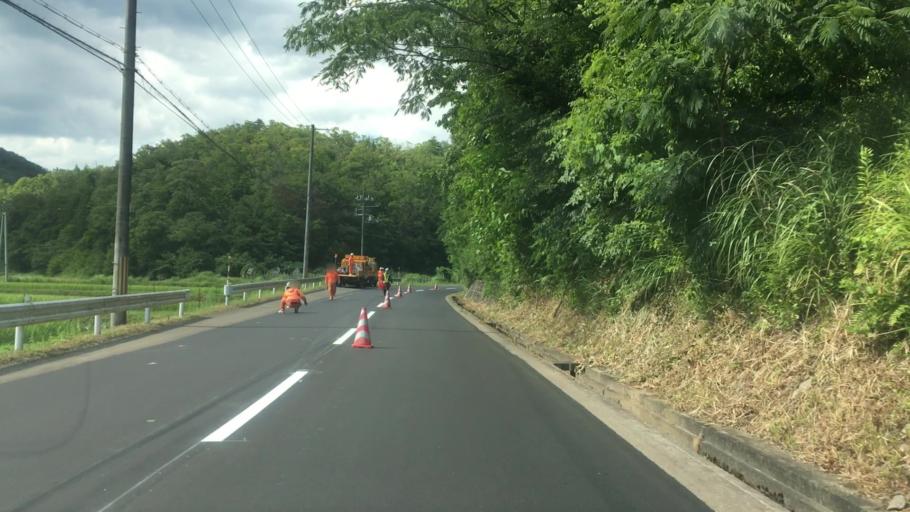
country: JP
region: Hyogo
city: Toyooka
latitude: 35.5045
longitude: 134.7772
